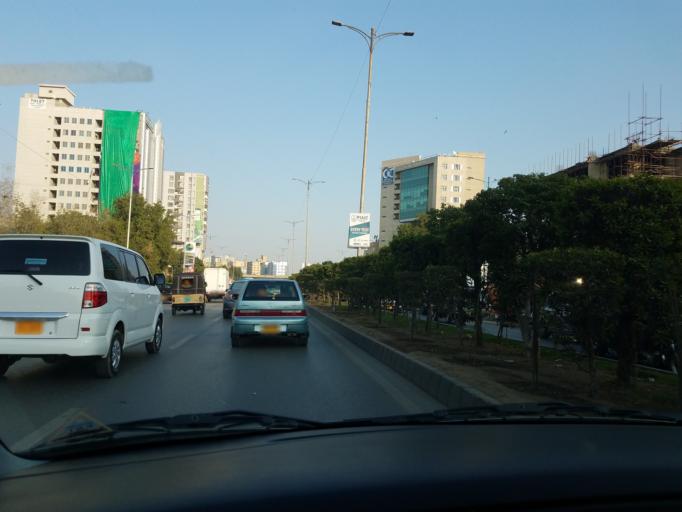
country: PK
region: Sindh
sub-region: Karachi District
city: Karachi
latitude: 24.8598
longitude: 67.0558
